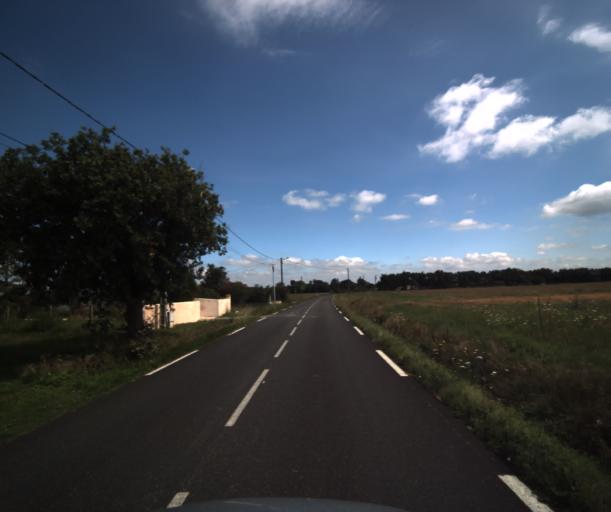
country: FR
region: Midi-Pyrenees
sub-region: Departement de la Haute-Garonne
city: Longages
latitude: 43.3820
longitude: 1.2457
